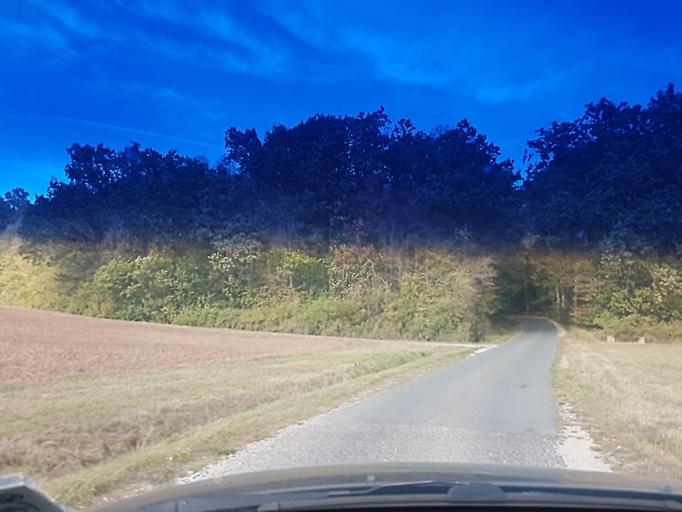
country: DE
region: Bavaria
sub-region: Regierungsbezirk Mittelfranken
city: Burghaslach
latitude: 49.7715
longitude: 10.5434
